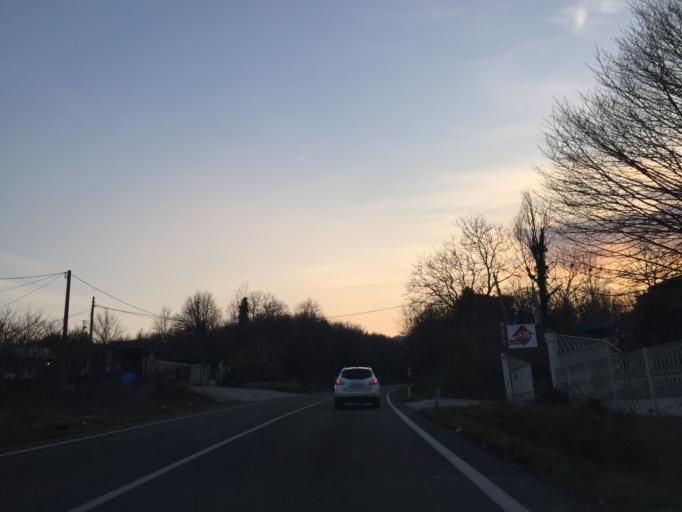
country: IT
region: Campania
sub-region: Provincia di Avellino
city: Avellino
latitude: 40.9041
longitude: 14.8077
